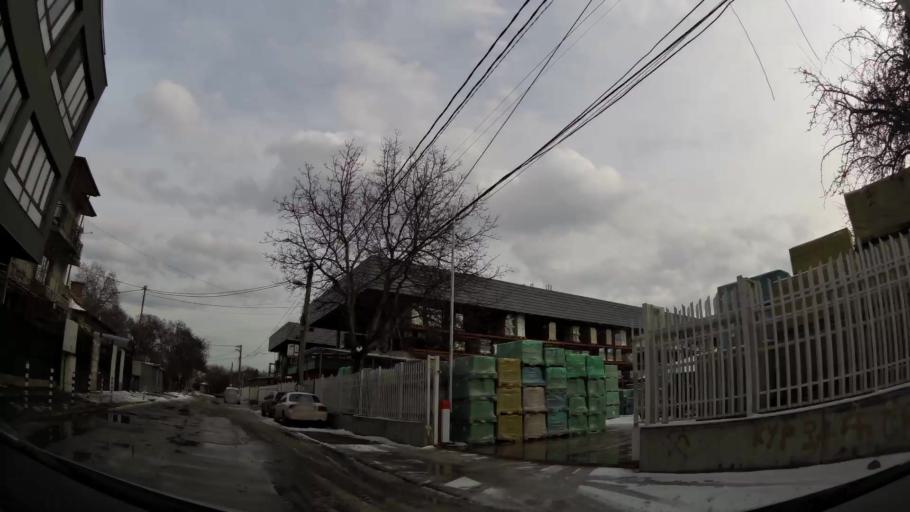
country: BG
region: Sofia-Capital
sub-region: Stolichna Obshtina
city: Sofia
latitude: 42.7033
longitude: 23.3810
